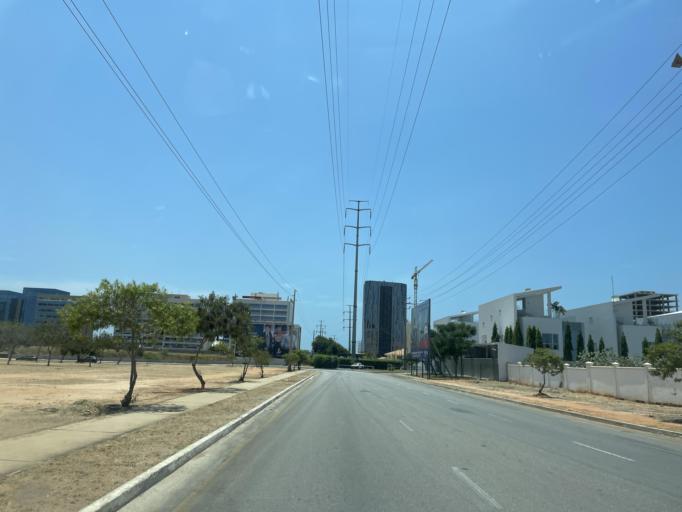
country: AO
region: Luanda
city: Luanda
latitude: -8.9199
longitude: 13.1911
